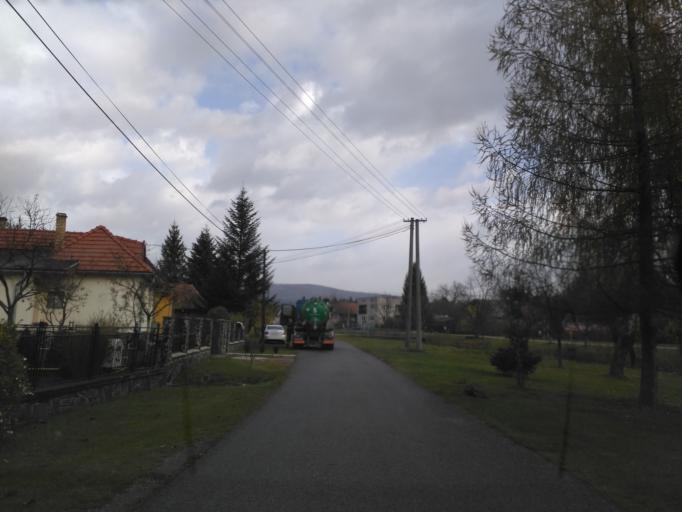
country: SK
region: Kosicky
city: Secovce
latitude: 48.7341
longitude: 21.4623
